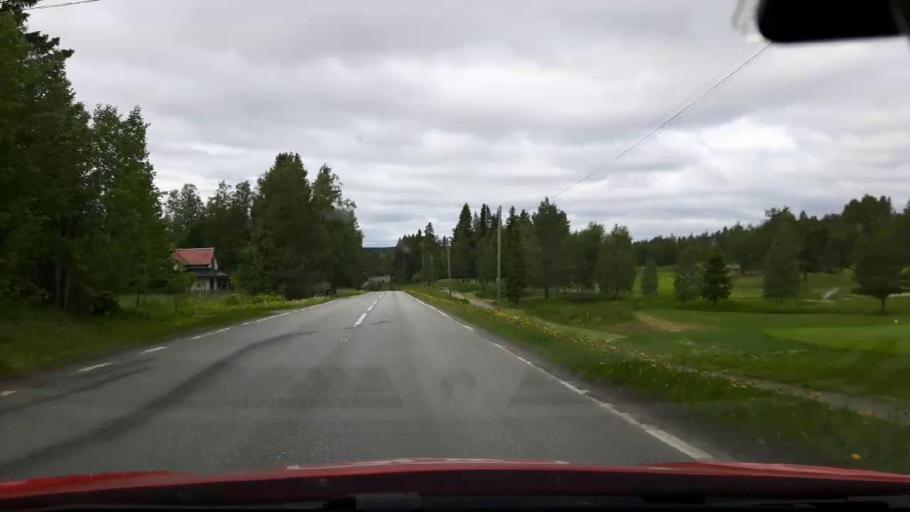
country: SE
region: Jaemtland
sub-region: Krokoms Kommun
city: Krokom
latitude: 63.2874
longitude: 14.5061
